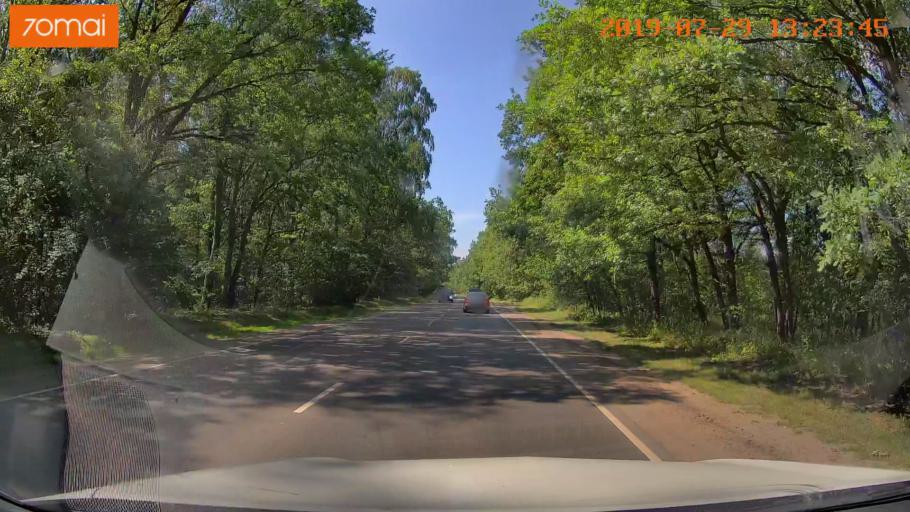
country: RU
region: Kaliningrad
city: Vzmorye
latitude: 54.7146
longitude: 20.3588
